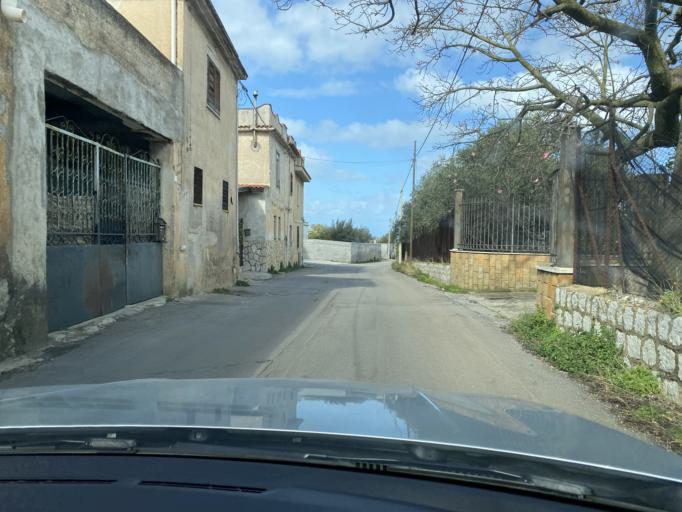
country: IT
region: Sicily
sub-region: Palermo
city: Carini
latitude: 38.1550
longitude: 13.1674
